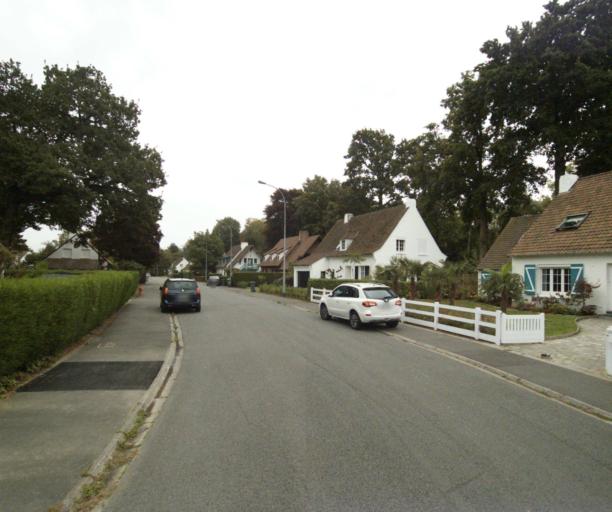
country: FR
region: Nord-Pas-de-Calais
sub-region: Departement du Nord
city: Lambersart
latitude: 50.6605
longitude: 3.0264
